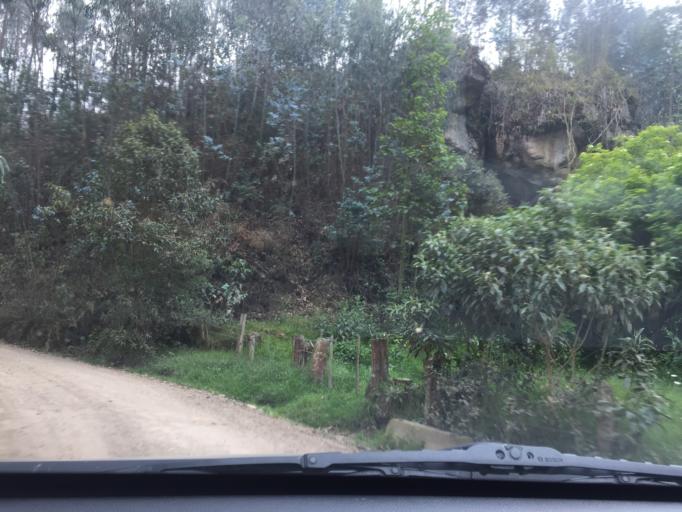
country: CO
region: Cundinamarca
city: Bojaca
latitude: 4.7150
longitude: -74.3501
